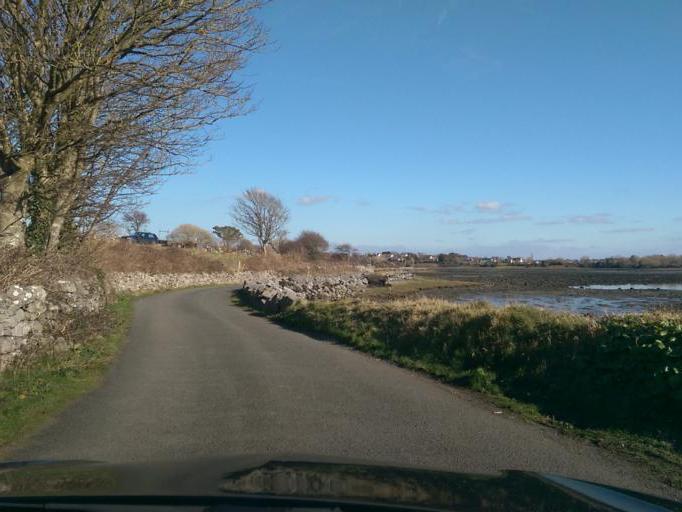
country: IE
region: Connaught
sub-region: County Galway
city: Oranmore
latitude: 53.2395
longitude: -8.9597
